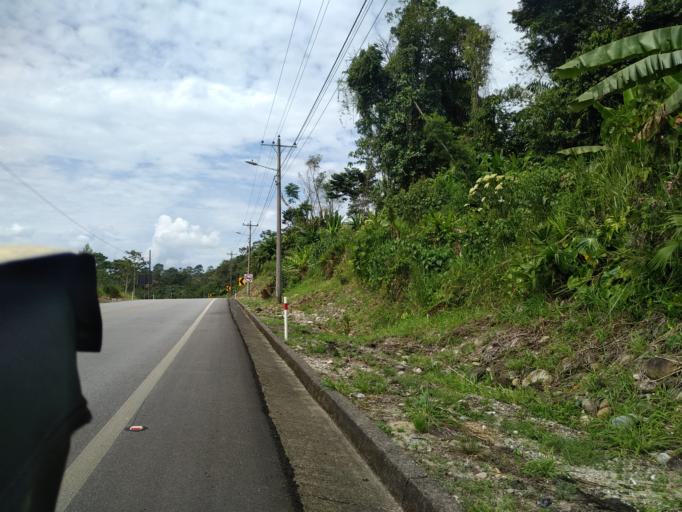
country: EC
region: Napo
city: Tena
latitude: -1.1416
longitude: -77.8382
